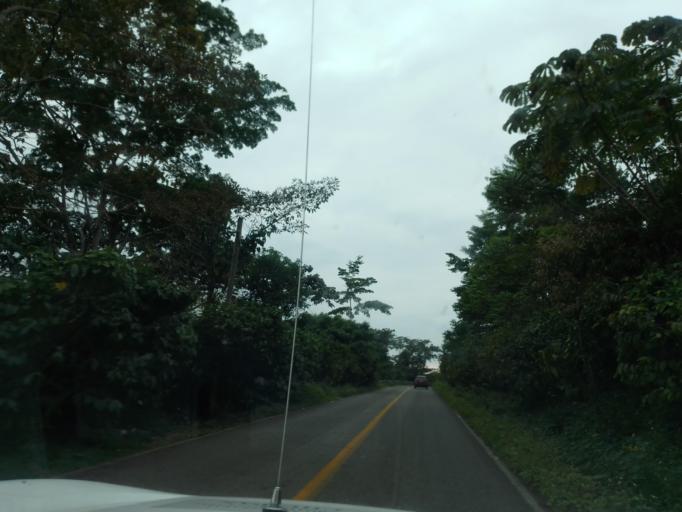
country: MX
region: Chiapas
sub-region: Union Juarez
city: Santo Domingo
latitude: 15.0381
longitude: -92.1269
